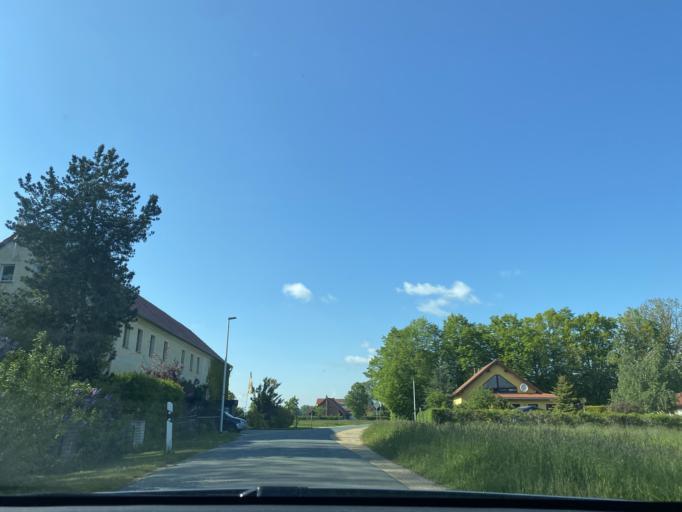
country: DE
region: Saxony
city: Reichenbach
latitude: 51.1019
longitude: 14.8315
